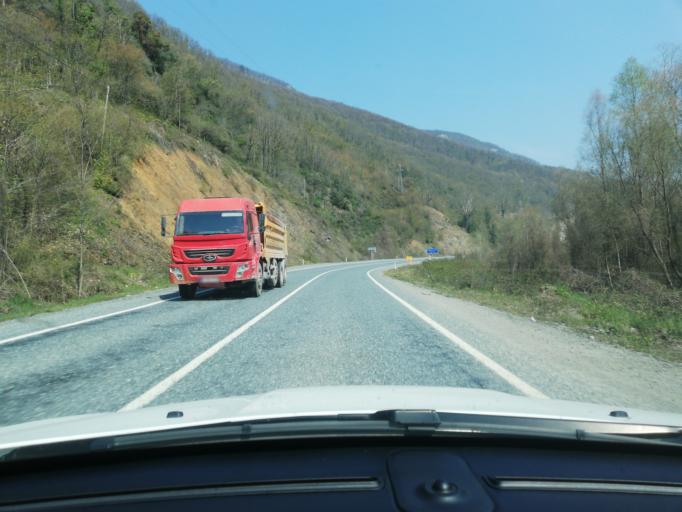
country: TR
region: Zonguldak
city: Gokcebey
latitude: 41.2660
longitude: 32.1603
